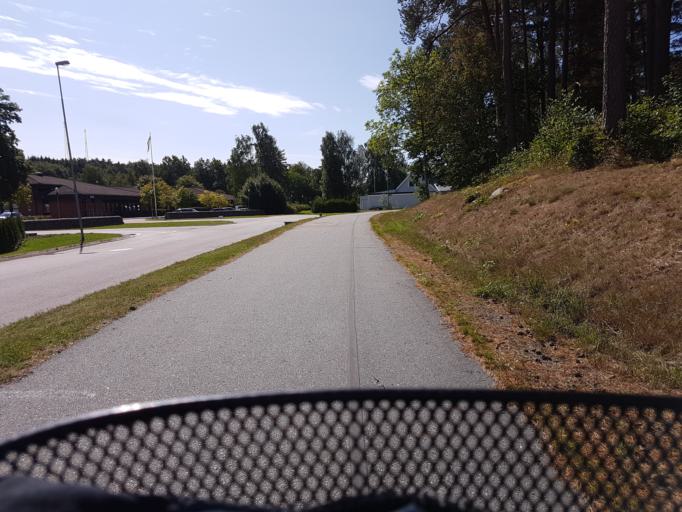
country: SE
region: Vaestra Goetaland
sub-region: Ale Kommun
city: Alvangen
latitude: 57.9465
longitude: 12.1072
